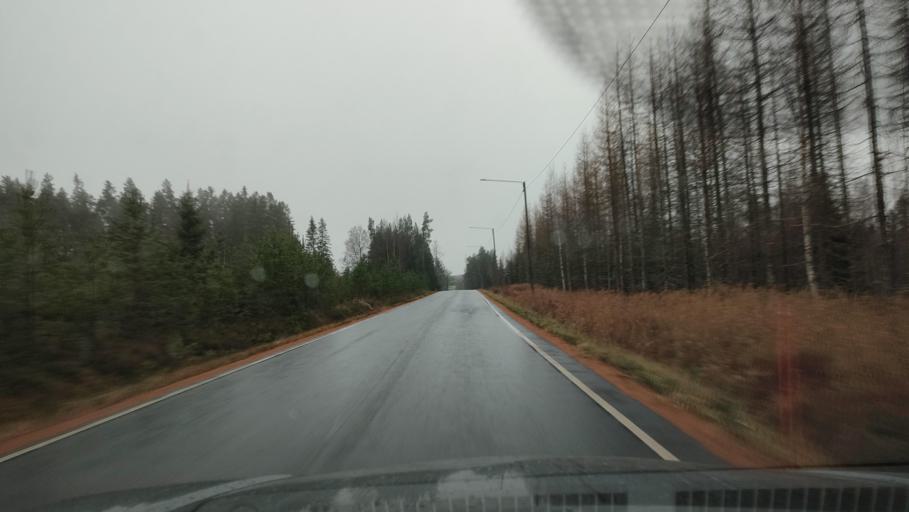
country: FI
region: Southern Ostrobothnia
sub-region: Suupohja
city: Karijoki
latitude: 62.1378
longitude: 21.6840
